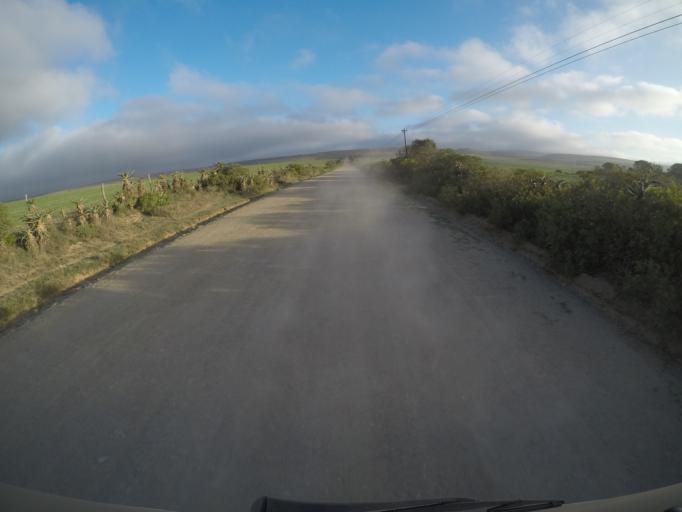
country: ZA
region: Western Cape
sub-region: Eden District Municipality
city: Mossel Bay
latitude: -34.1145
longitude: 22.0533
